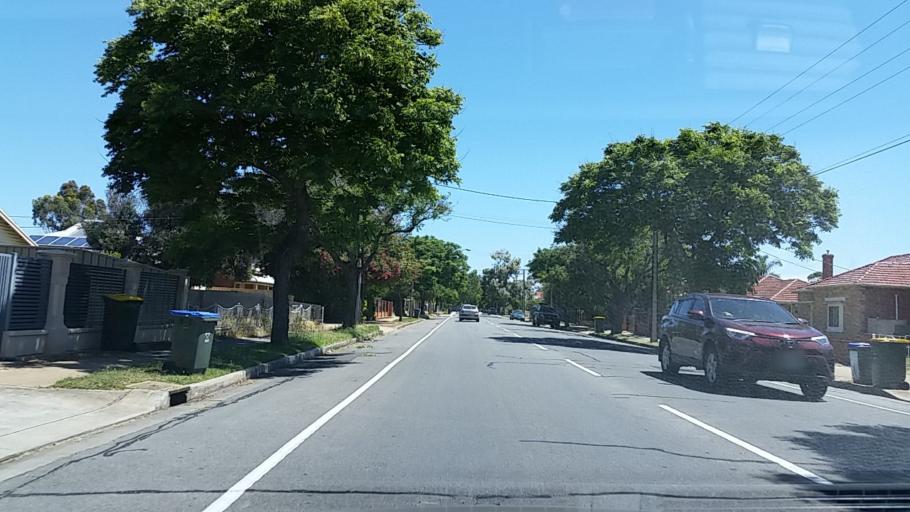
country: AU
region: South Australia
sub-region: Charles Sturt
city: Woodville
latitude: -34.8854
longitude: 138.5627
